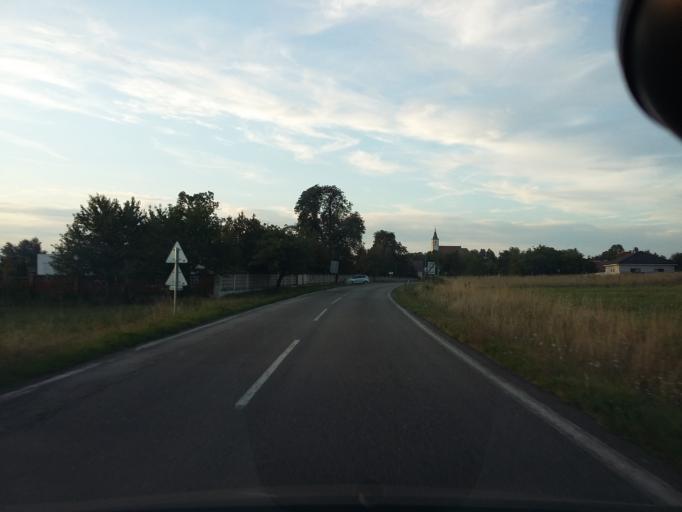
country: SK
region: Bratislavsky
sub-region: Okres Malacky
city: Malacky
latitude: 48.4016
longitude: 17.1550
